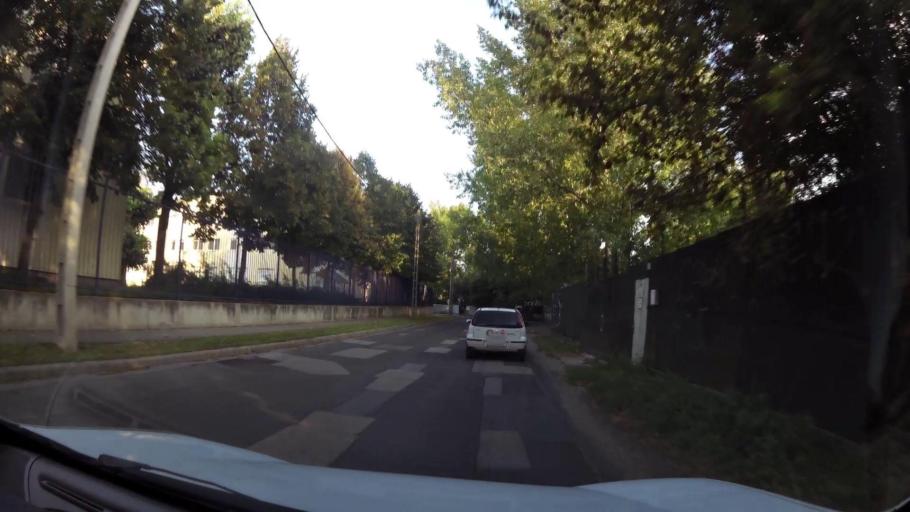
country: HU
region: Budapest
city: Budapest XVI. keruelet
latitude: 47.5026
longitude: 19.1716
